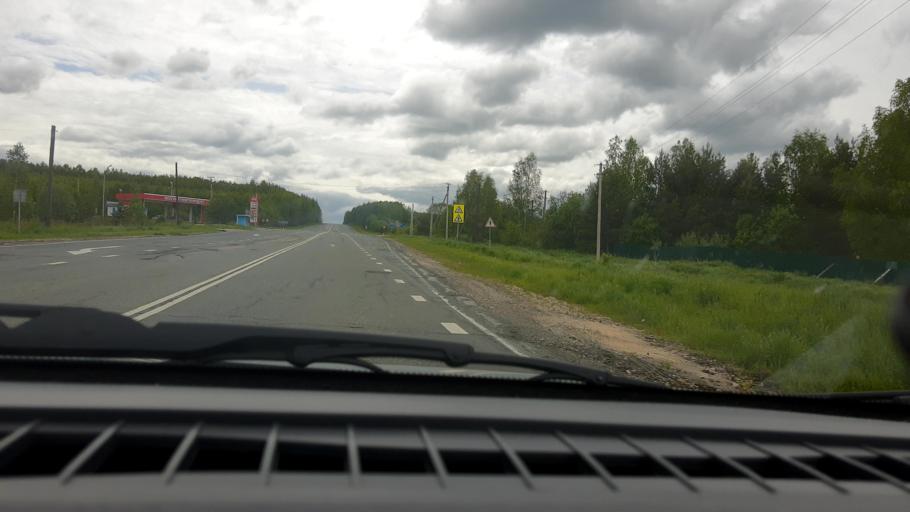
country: RU
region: Nizjnij Novgorod
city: Vladimirskoye
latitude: 56.9736
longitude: 45.1128
